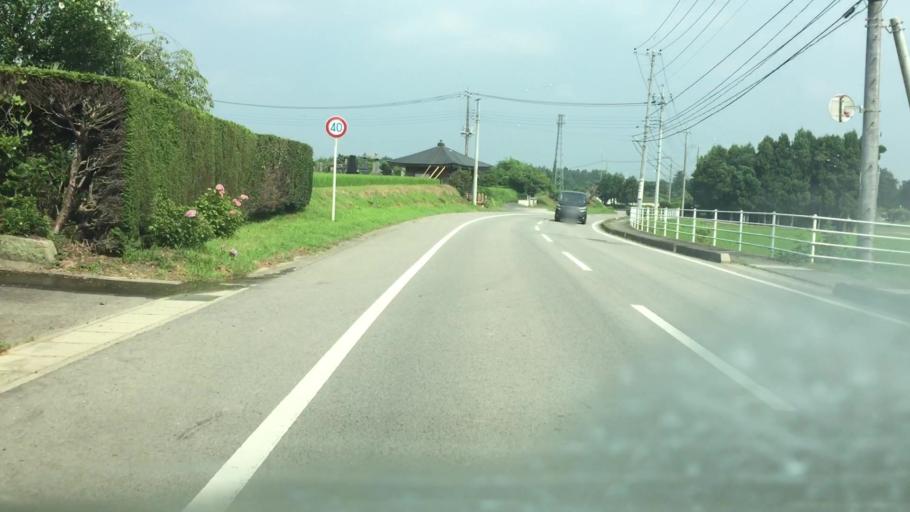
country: JP
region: Tochigi
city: Kuroiso
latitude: 36.9735
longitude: 139.9640
